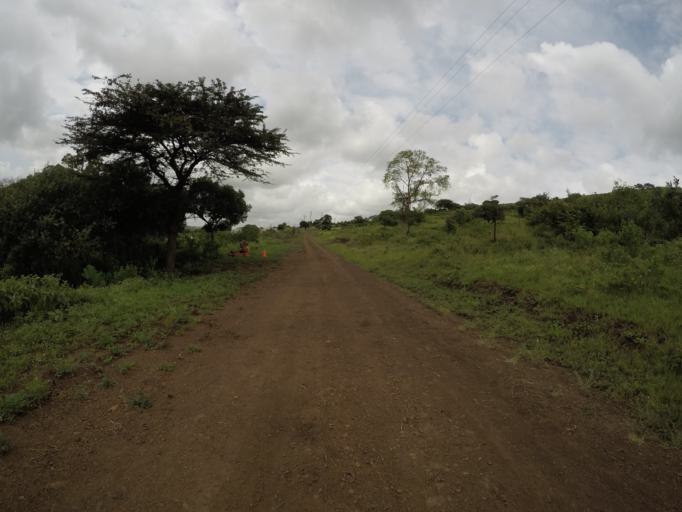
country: ZA
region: KwaZulu-Natal
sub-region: uThungulu District Municipality
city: Empangeni
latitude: -28.5859
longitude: 31.8890
